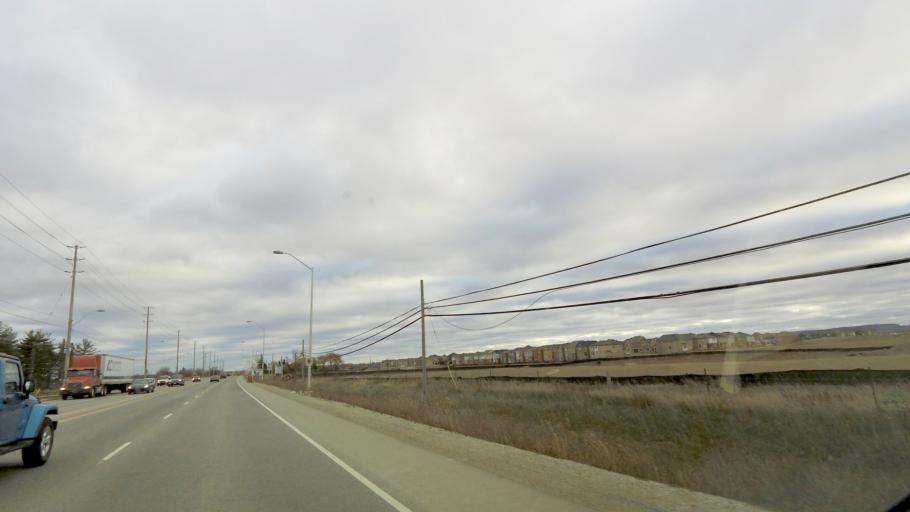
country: CA
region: Ontario
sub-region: Halton
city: Milton
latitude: 43.4916
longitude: -79.8414
